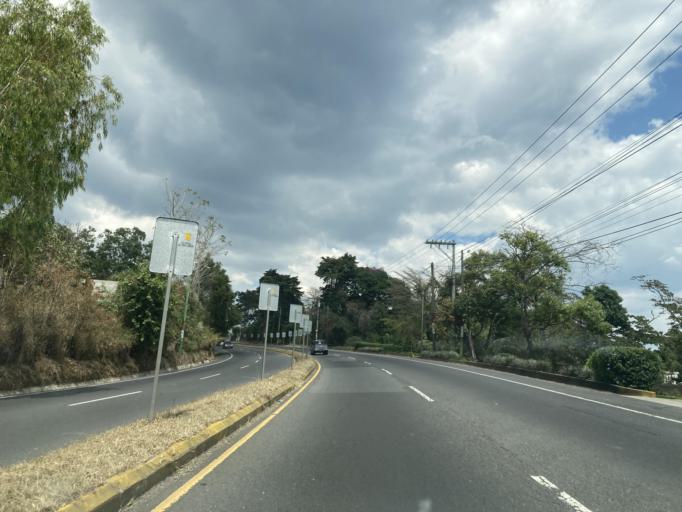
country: GT
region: Guatemala
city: Fraijanes
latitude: 14.4417
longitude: -90.4742
